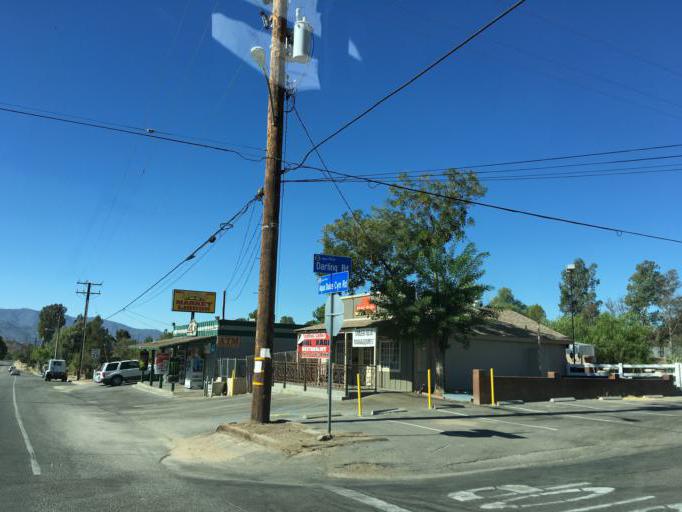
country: US
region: California
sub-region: Los Angeles County
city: Agua Dulce
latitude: 34.4964
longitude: -118.3262
